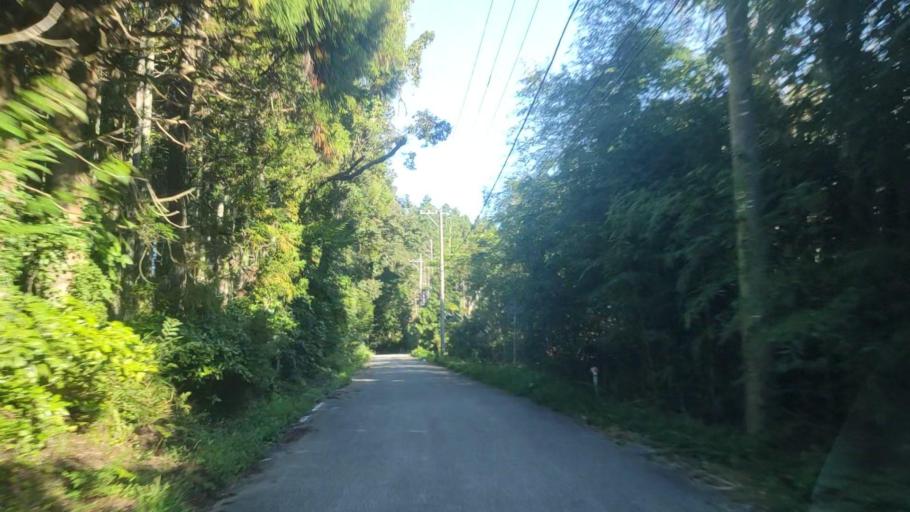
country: JP
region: Ishikawa
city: Nanao
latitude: 37.1341
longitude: 136.9099
